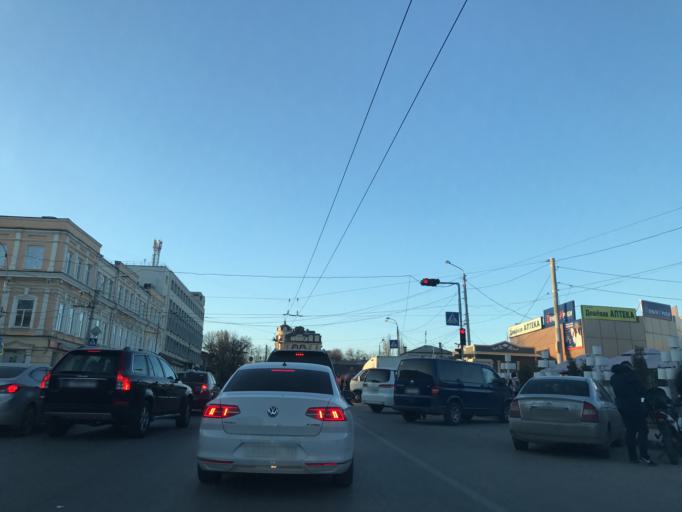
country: RU
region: Rostov
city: Rostov-na-Donu
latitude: 47.2318
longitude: 39.7616
